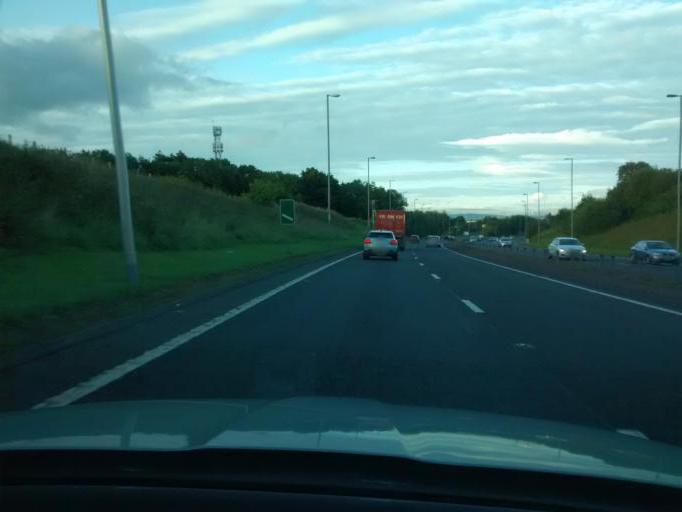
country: GB
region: Scotland
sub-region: Renfrewshire
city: Johnstone
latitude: 55.8362
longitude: -4.5264
